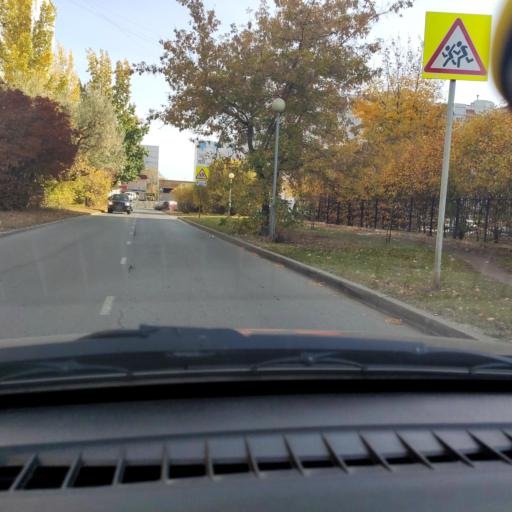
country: RU
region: Samara
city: Tol'yatti
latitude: 53.5017
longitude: 49.2852
